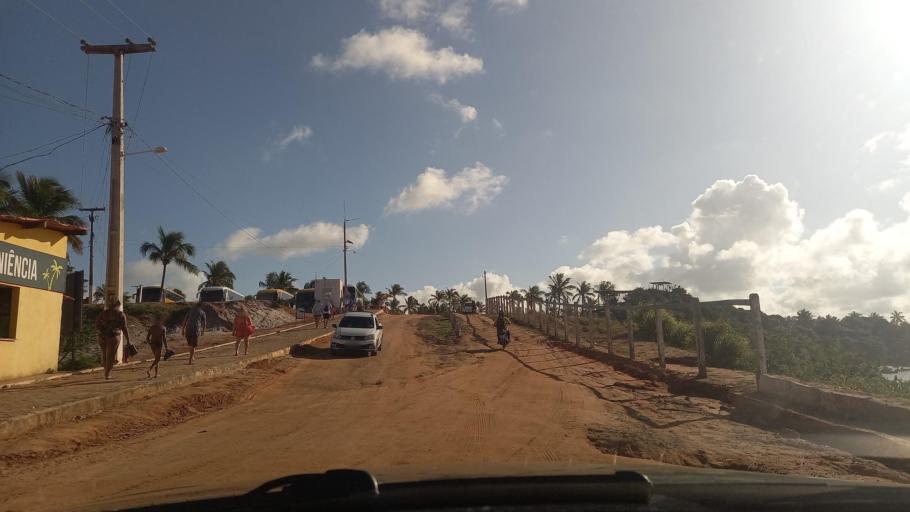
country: BR
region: Alagoas
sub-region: Marechal Deodoro
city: Marechal Deodoro
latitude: -9.8609
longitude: -35.9066
